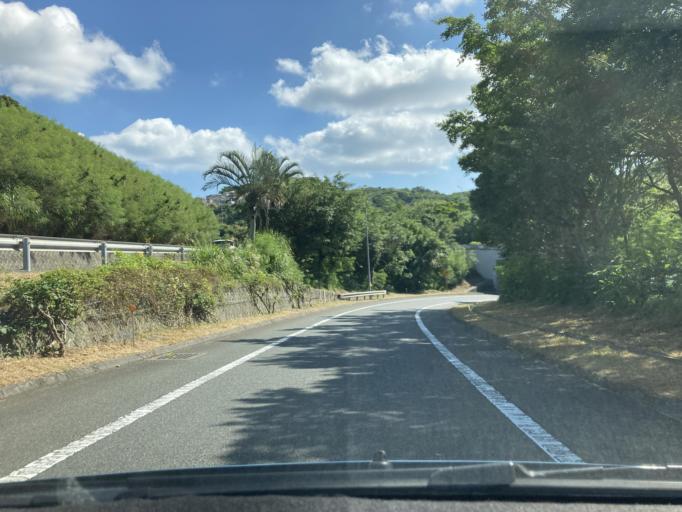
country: JP
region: Okinawa
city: Ginowan
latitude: 26.2485
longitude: 127.7499
